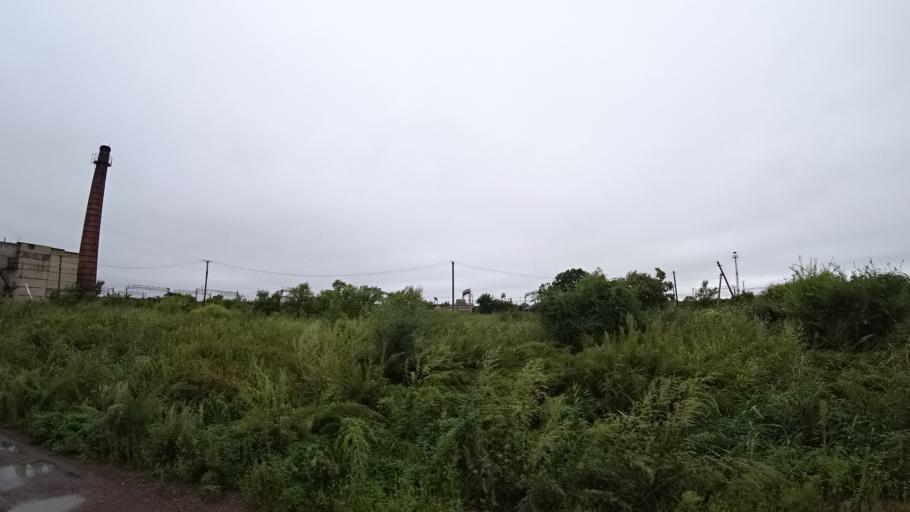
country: RU
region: Primorskiy
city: Monastyrishche
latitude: 44.2113
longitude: 132.4441
